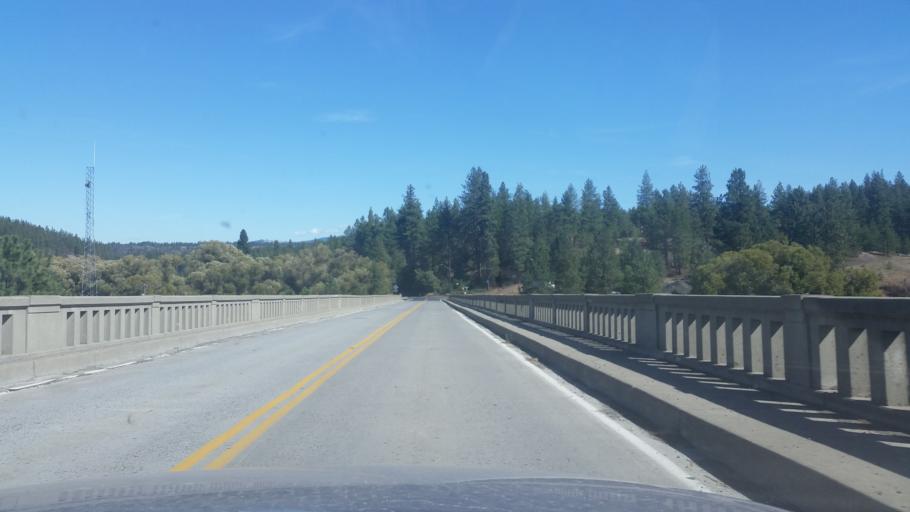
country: US
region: Washington
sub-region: Spokane County
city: Spokane
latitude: 47.5667
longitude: -117.4940
